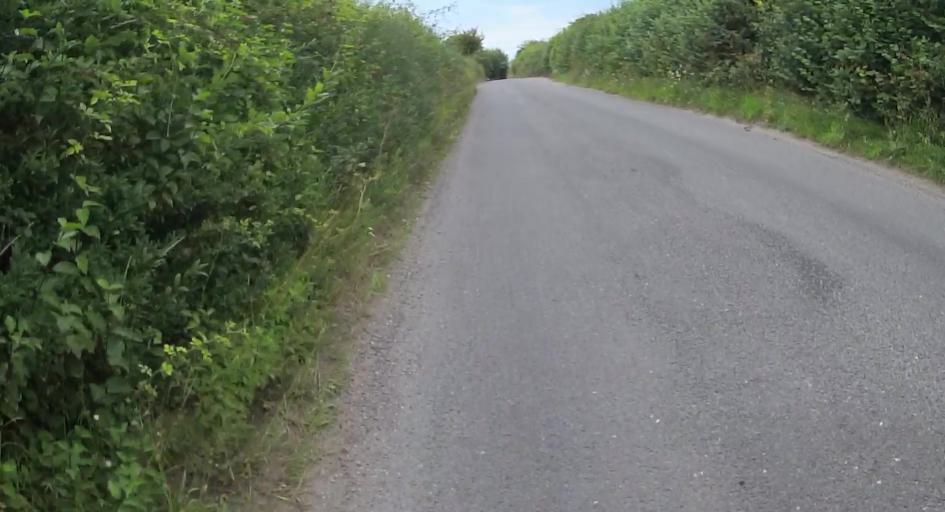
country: GB
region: England
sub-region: Hampshire
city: Overton
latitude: 51.1925
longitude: -1.2481
